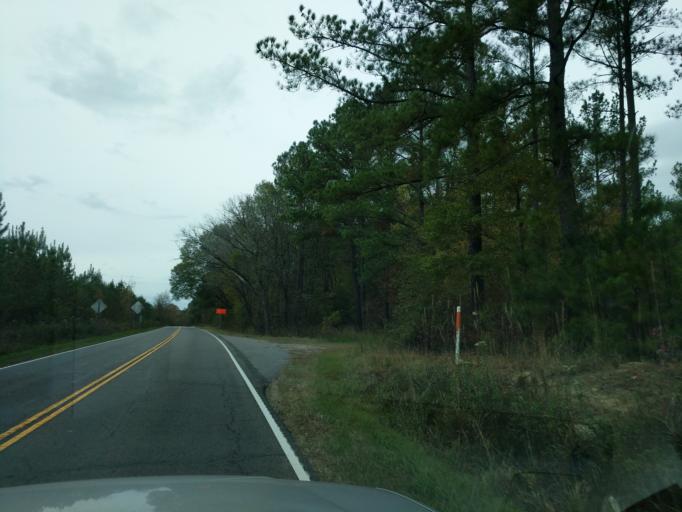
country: US
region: South Carolina
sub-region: Lexington County
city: Batesburg
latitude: 33.9424
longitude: -81.6167
